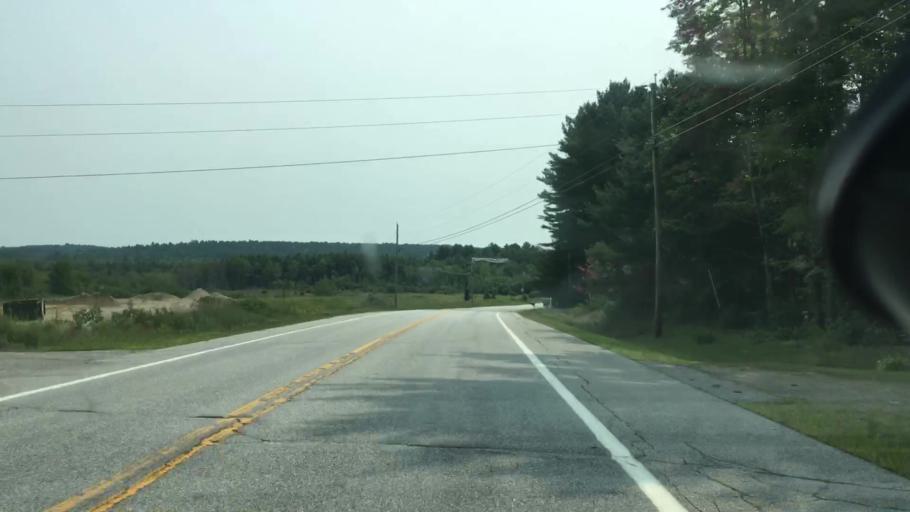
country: US
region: Maine
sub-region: Kennebec County
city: Wayne
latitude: 44.3964
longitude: -70.1189
